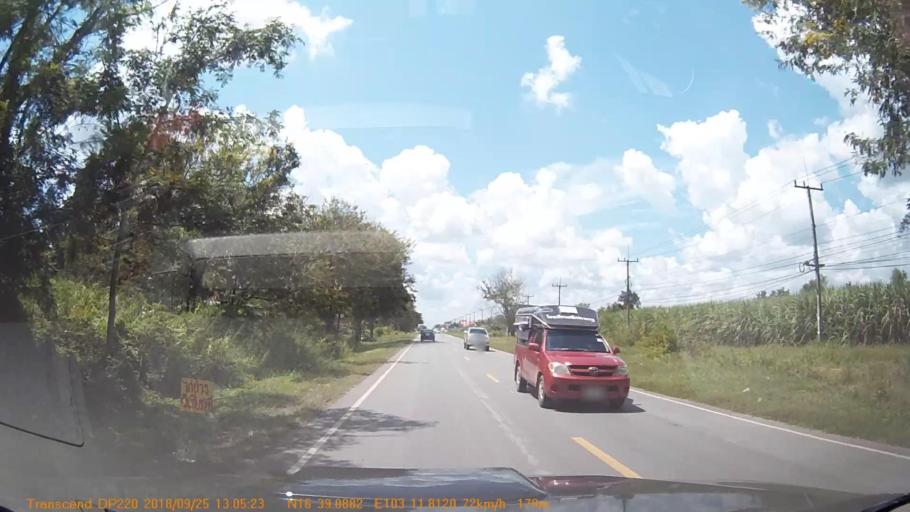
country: TH
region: Kalasin
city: Huai Mek
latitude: 16.6515
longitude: 103.1969
